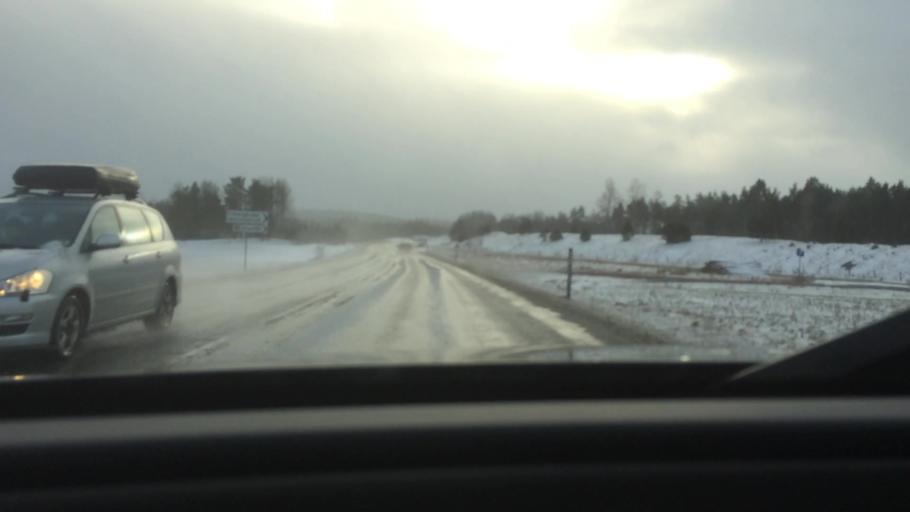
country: SE
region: Vaestra Goetaland
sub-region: Falkopings Kommun
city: Falkoeping
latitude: 57.9771
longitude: 13.5277
